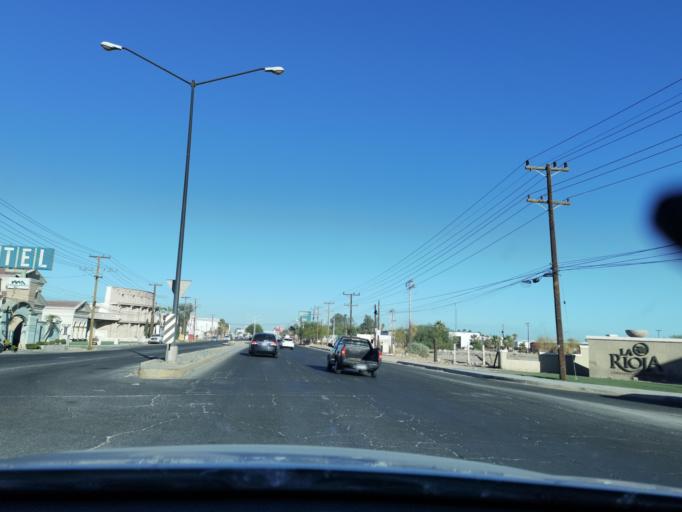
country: MX
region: Baja California
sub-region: Mexicali
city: Islas Agrarias Grupo A
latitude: 32.6530
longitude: -115.3668
